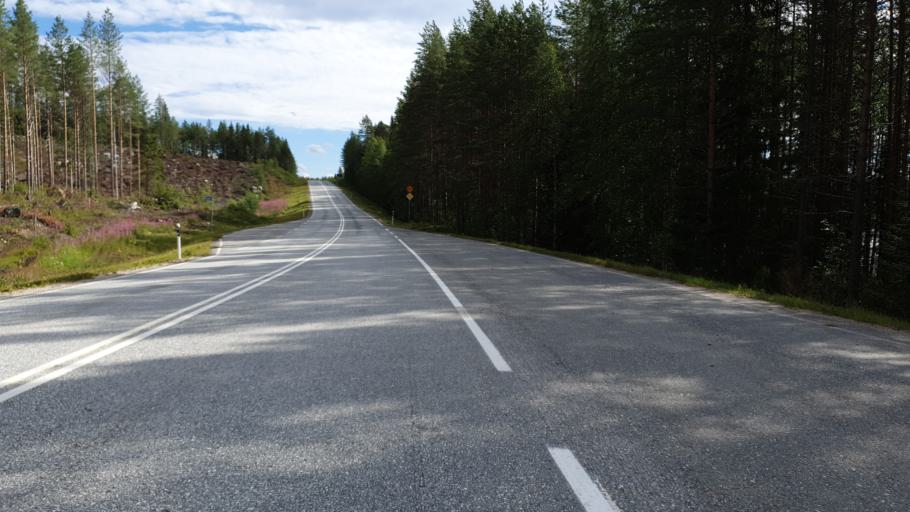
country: FI
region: Kainuu
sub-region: Kehys-Kainuu
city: Kuhmo
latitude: 64.4939
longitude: 29.9010
